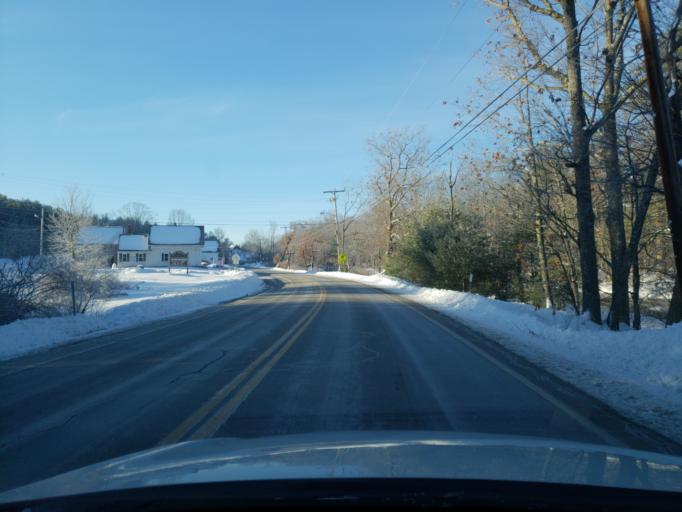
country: US
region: New Hampshire
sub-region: Hillsborough County
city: New Boston
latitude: 42.9797
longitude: -71.6890
